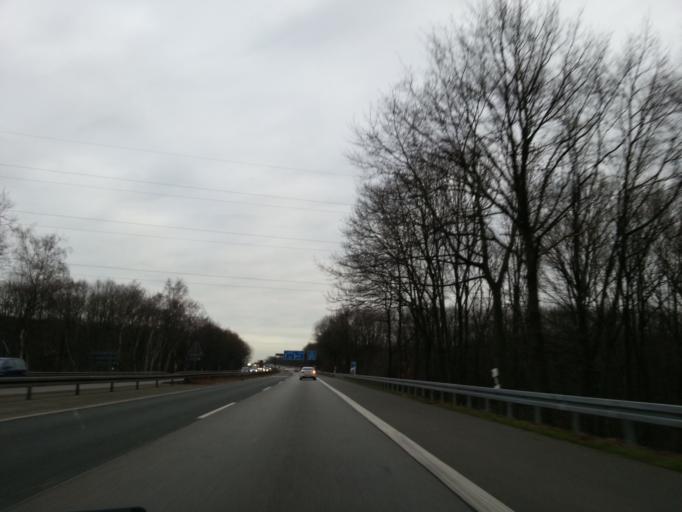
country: DE
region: North Rhine-Westphalia
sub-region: Regierungsbezirk Dusseldorf
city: Dinslaken
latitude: 51.5429
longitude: 6.8260
